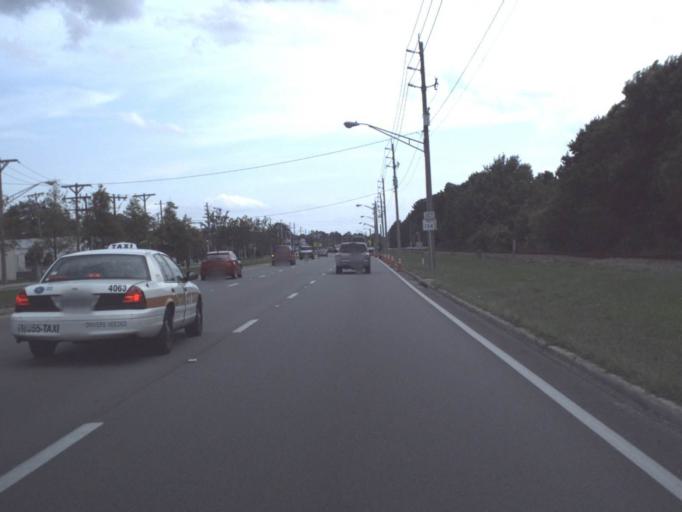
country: US
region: Florida
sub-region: Clay County
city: Bellair-Meadowbrook Terrace
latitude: 30.2514
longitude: -81.6988
